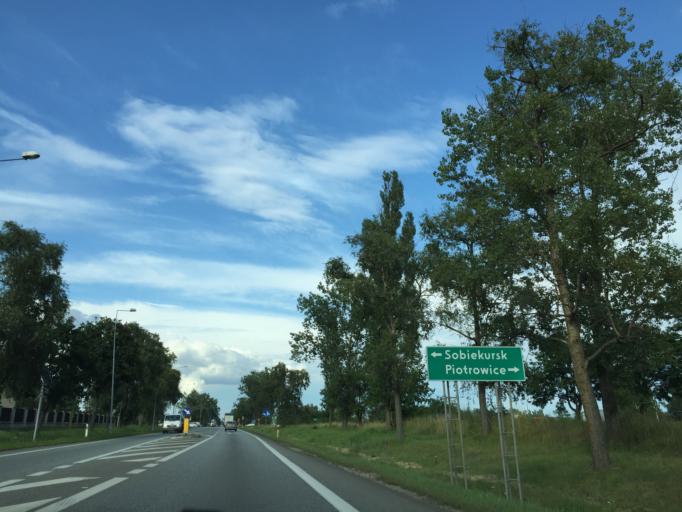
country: PL
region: Masovian Voivodeship
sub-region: Powiat otwocki
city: Karczew
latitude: 52.0149
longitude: 21.2856
